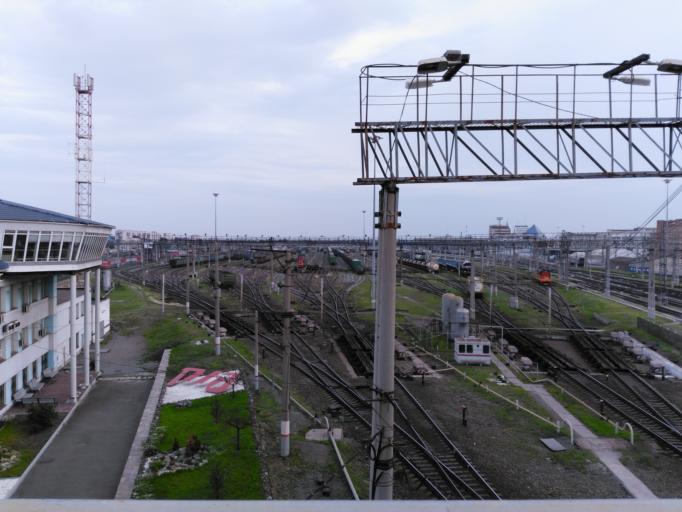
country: RU
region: Chelyabinsk
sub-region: Gorod Chelyabinsk
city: Chelyabinsk
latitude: 55.1461
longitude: 61.4220
